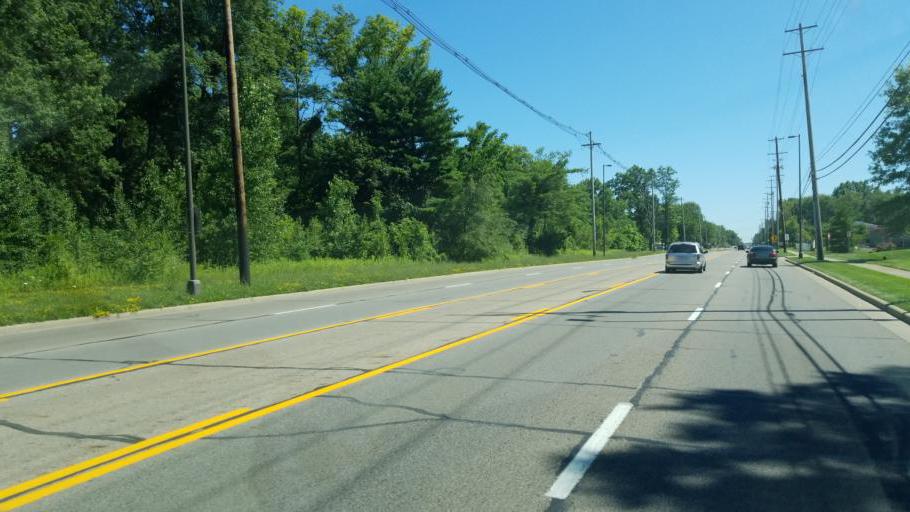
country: US
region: Ohio
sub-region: Franklin County
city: Gahanna
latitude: 40.0254
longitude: -82.9110
